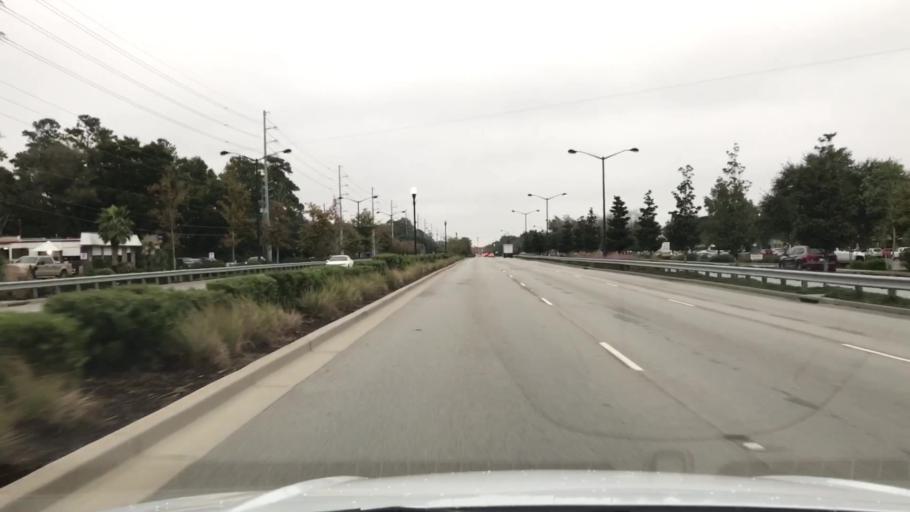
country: US
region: South Carolina
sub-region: Charleston County
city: Mount Pleasant
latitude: 32.8069
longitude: -79.8832
